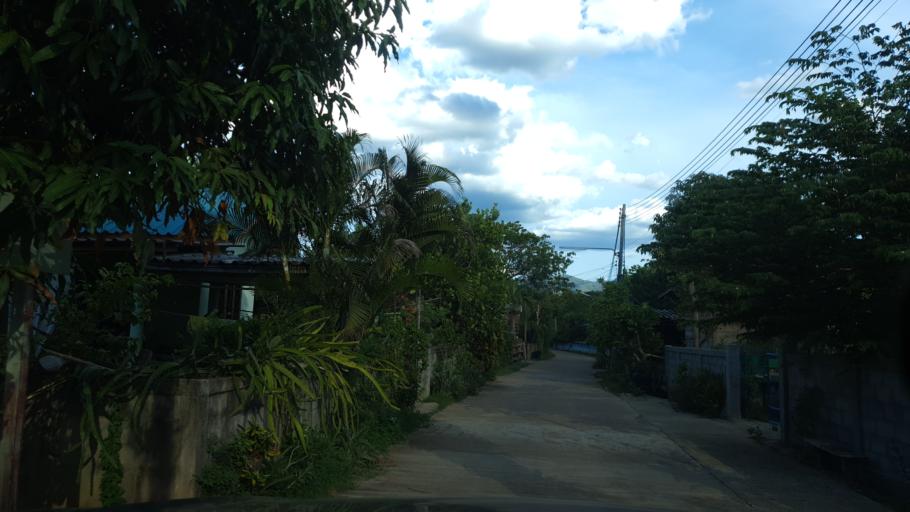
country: TH
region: Lampang
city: Sop Prap
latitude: 17.8710
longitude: 99.3070
